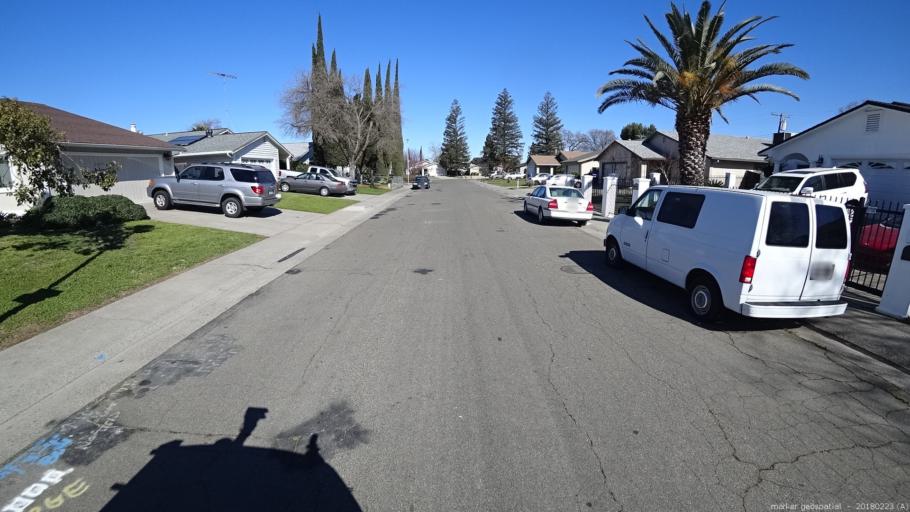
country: US
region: California
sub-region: Sacramento County
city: North Highlands
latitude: 38.7059
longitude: -121.3949
